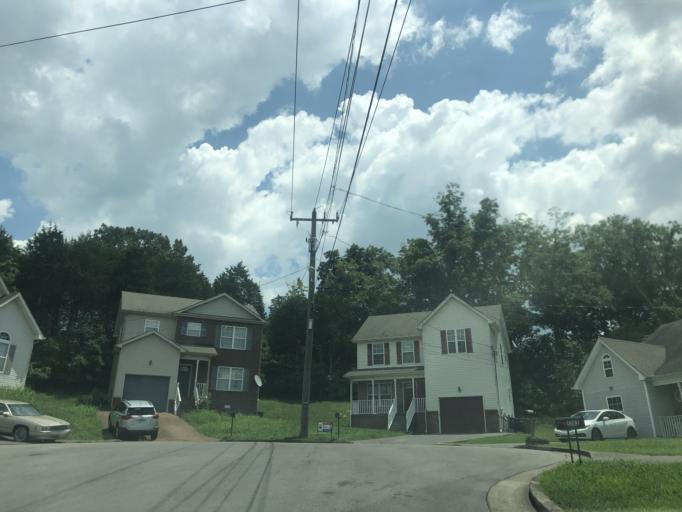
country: US
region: Tennessee
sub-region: Rutherford County
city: La Vergne
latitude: 36.0594
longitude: -86.6524
